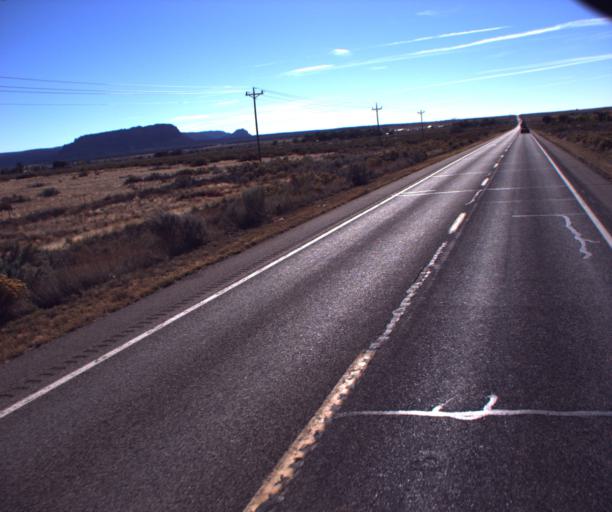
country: US
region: Arizona
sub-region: Mohave County
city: Colorado City
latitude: 36.9377
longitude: -112.9489
